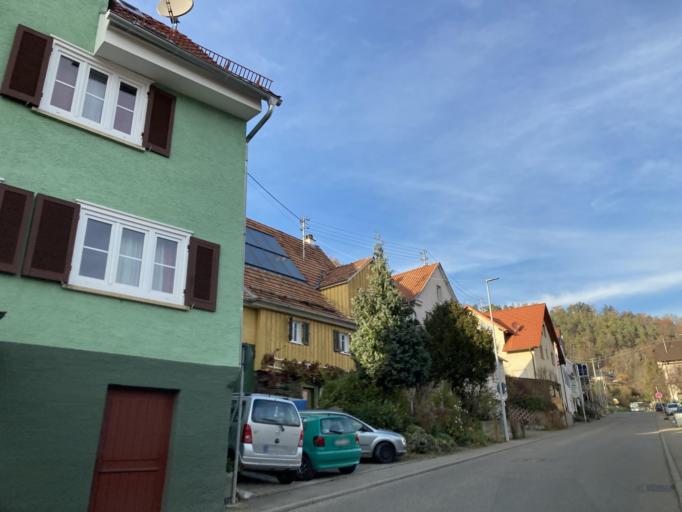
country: DE
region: Baden-Wuerttemberg
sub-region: Tuebingen Region
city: Hirrlingen
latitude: 48.4587
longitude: 8.8701
